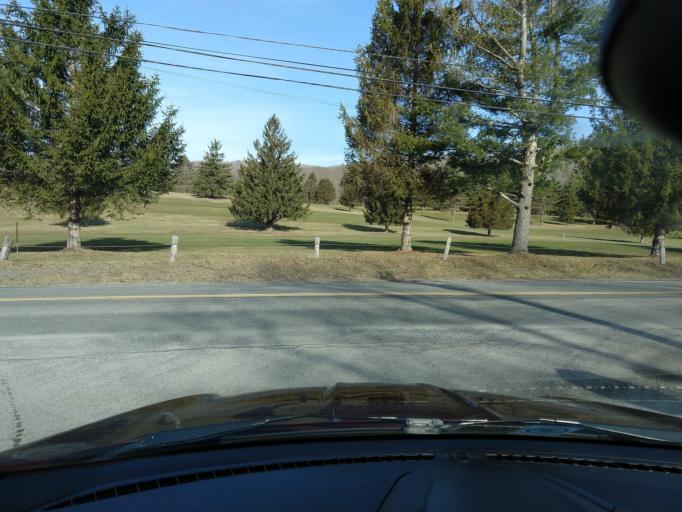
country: US
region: West Virginia
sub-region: Pocahontas County
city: Marlinton
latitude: 38.2029
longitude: -80.1105
